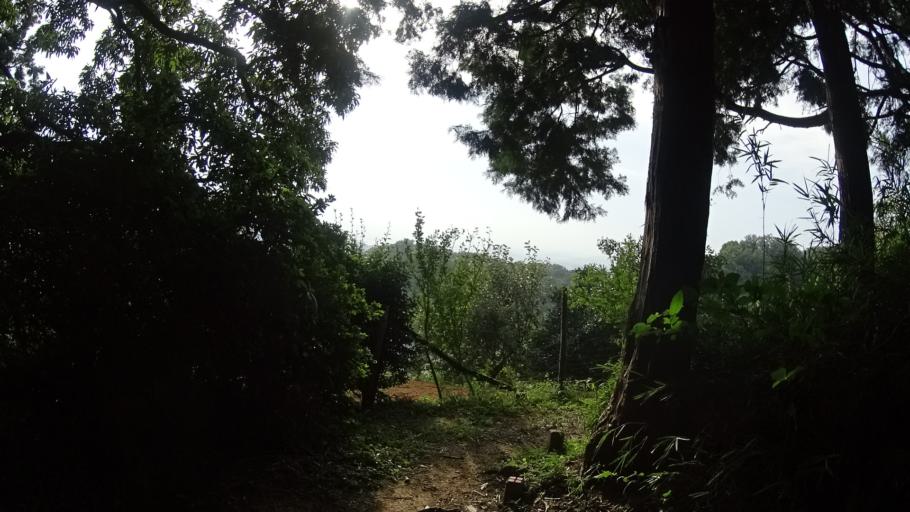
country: JP
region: Kanagawa
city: Zushi
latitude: 35.3557
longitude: 139.6018
